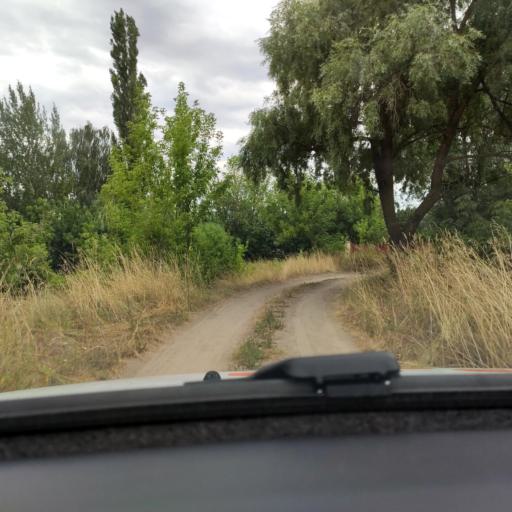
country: RU
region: Voronezj
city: Orlovo
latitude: 51.6480
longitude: 39.5671
